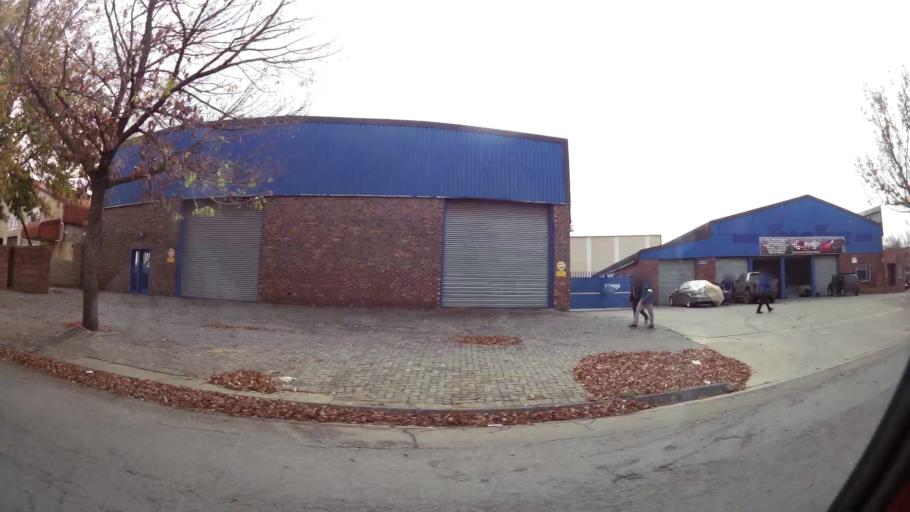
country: ZA
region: Gauteng
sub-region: Sedibeng District Municipality
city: Vanderbijlpark
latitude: -26.7057
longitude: 27.8540
